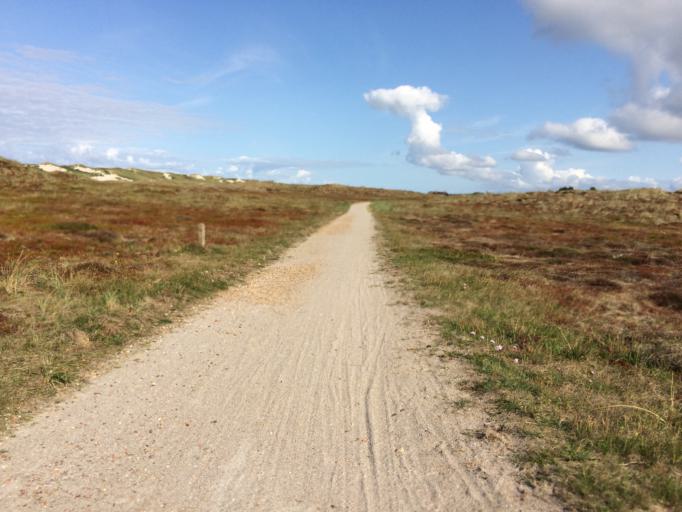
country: DK
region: Central Jutland
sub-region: Ringkobing-Skjern Kommune
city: Hvide Sande
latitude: 55.8989
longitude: 8.1597
